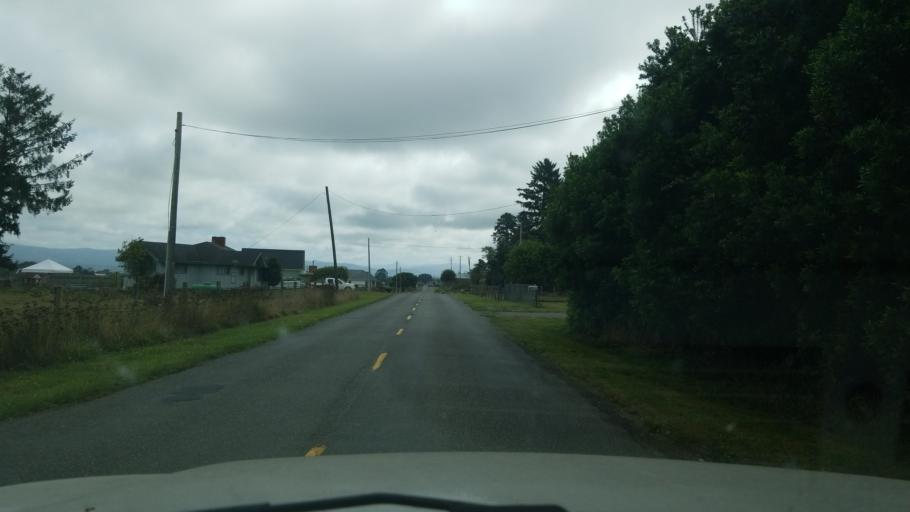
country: US
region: California
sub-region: Humboldt County
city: Ferndale
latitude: 40.5810
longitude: -124.2802
